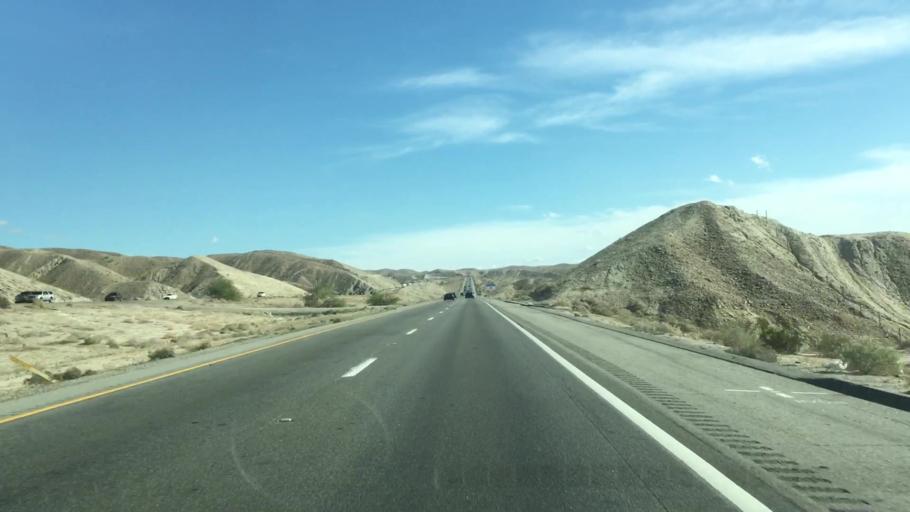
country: US
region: California
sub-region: Riverside County
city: Coachella
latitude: 33.7011
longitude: -116.1199
